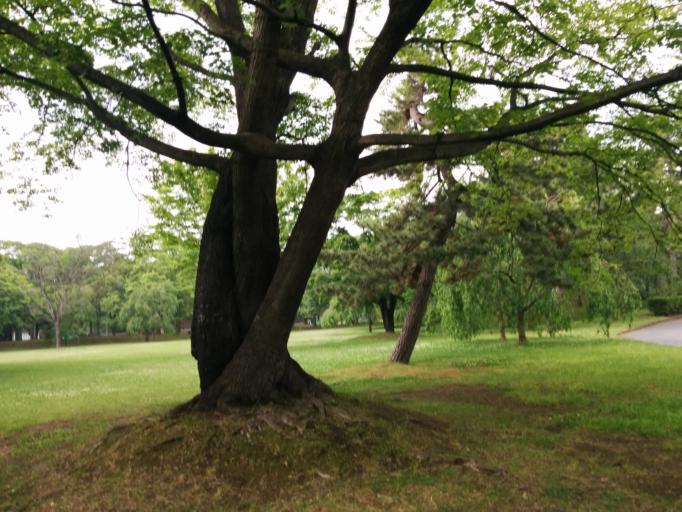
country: JP
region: Aomori
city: Hirosaki
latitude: 40.6053
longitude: 140.4634
